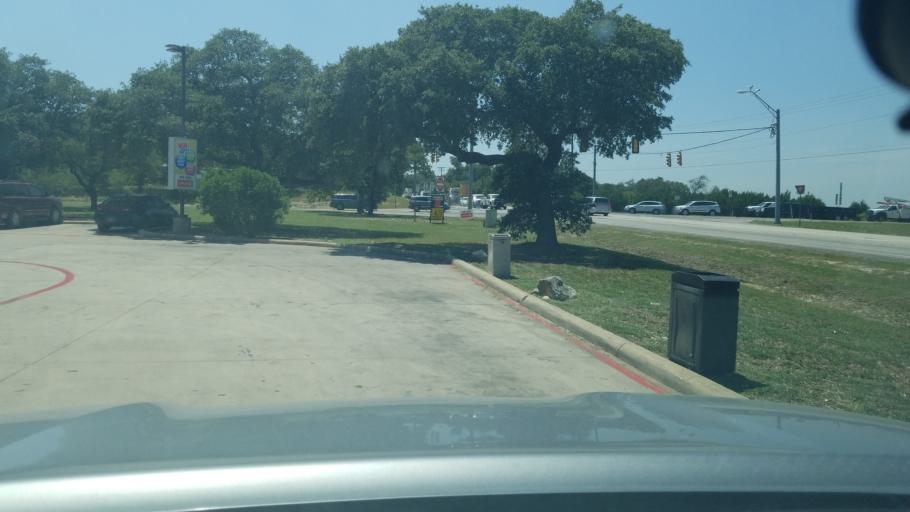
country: US
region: Texas
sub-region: Bexar County
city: Fair Oaks Ranch
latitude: 29.8270
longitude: -98.5721
